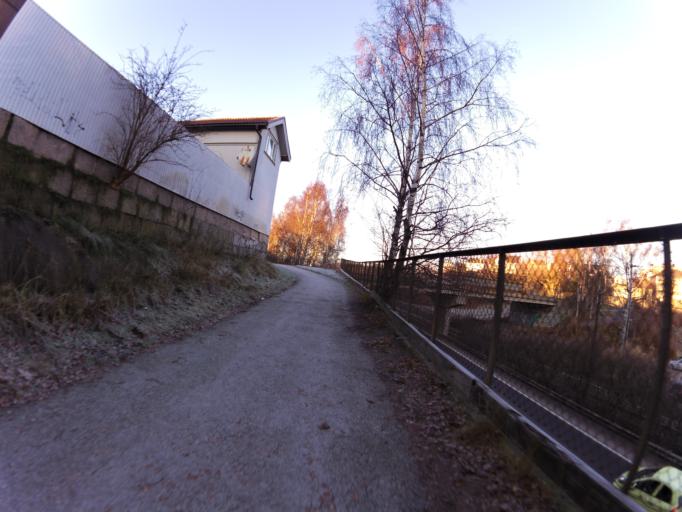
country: NO
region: Ostfold
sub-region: Fredrikstad
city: Fredrikstad
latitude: 59.2139
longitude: 10.9443
